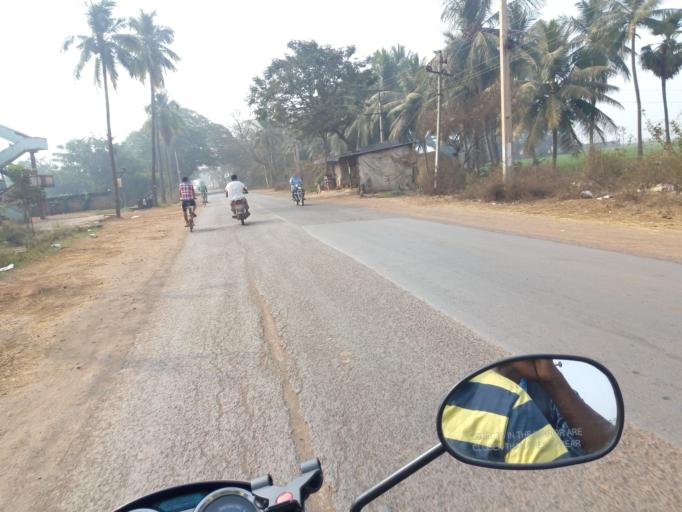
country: IN
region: Andhra Pradesh
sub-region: West Godavari
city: Tadepallegudem
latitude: 16.8133
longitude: 81.4082
